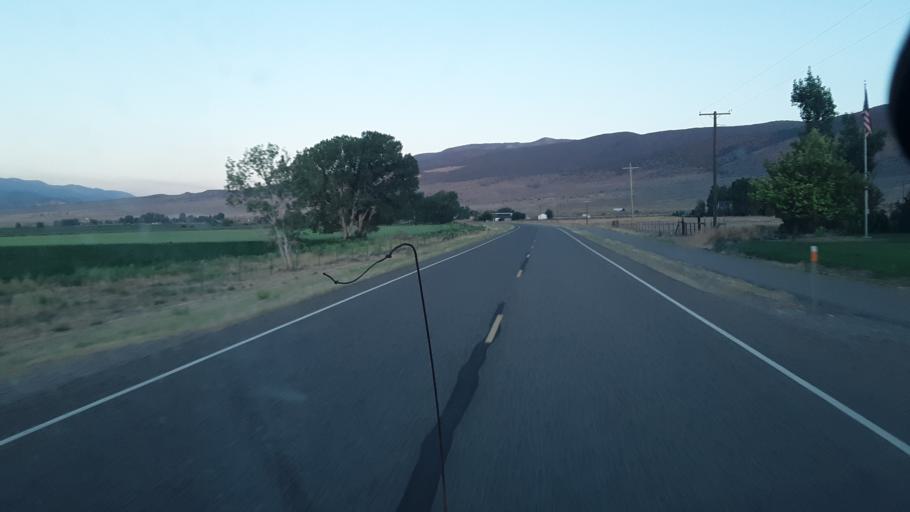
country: US
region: Utah
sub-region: Sevier County
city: Monroe
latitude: 38.6537
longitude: -112.1980
